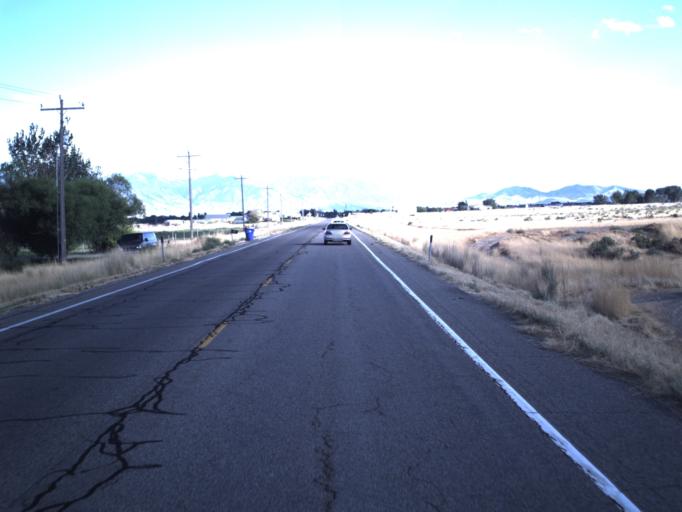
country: US
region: Utah
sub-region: Tooele County
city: Grantsville
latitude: 40.6107
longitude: -112.4932
